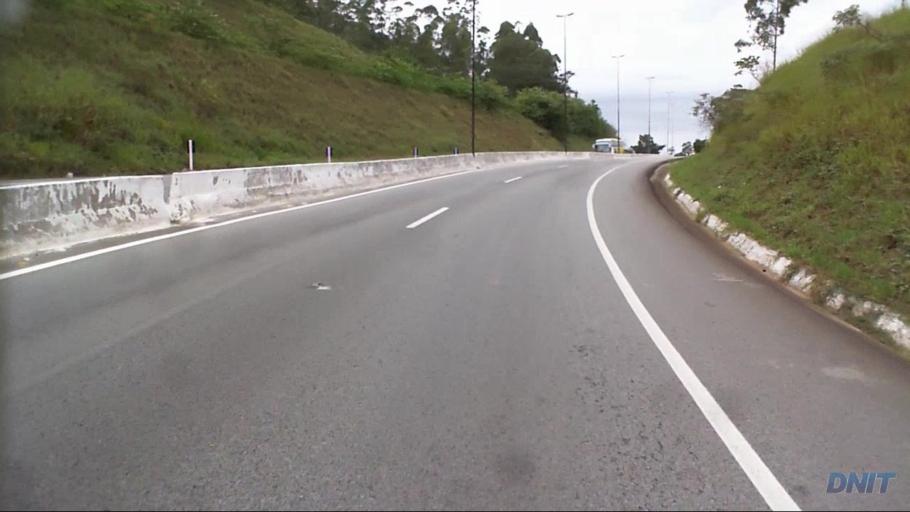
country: BR
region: Minas Gerais
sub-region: Nova Era
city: Nova Era
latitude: -19.7614
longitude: -43.0466
